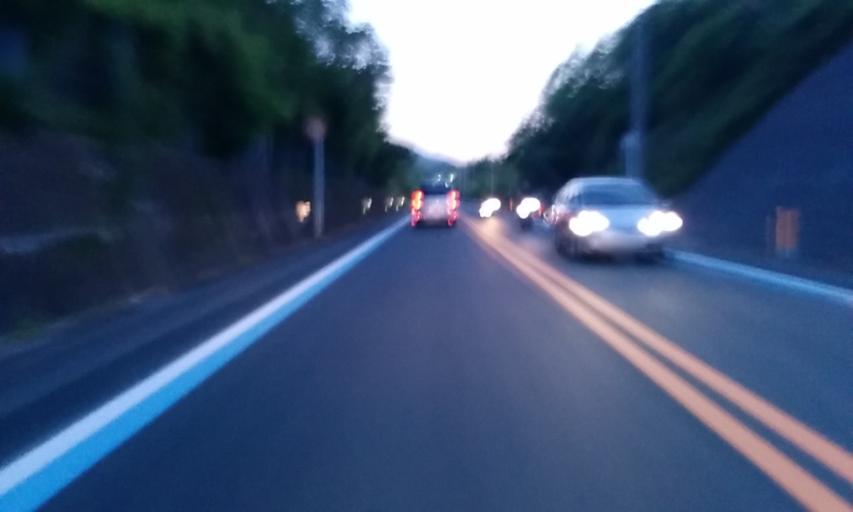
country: JP
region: Ehime
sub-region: Nishiuwa-gun
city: Ikata-cho
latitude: 33.5375
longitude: 132.4020
